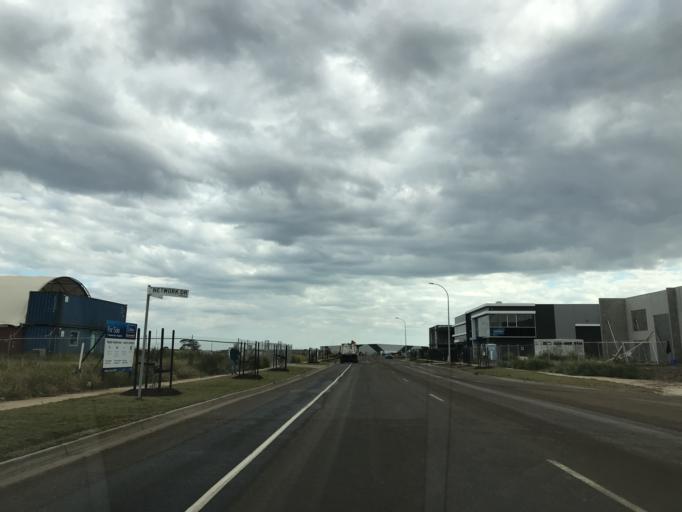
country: AU
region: Victoria
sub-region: Wyndham
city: Truganina
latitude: -37.8268
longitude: 144.7443
